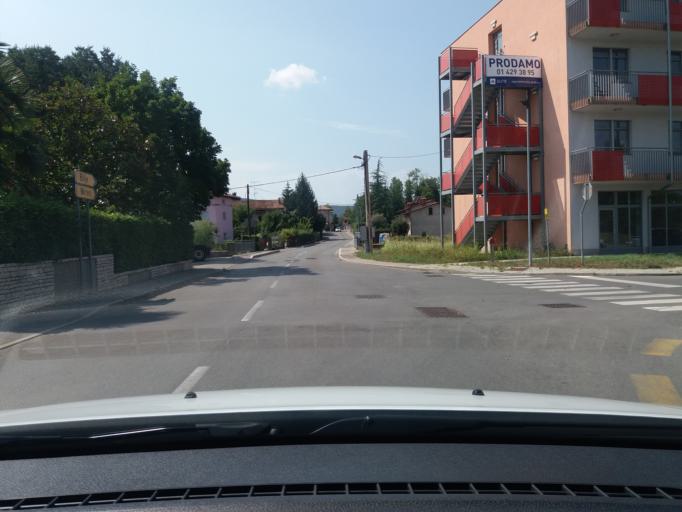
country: SI
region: Sempeter-Vrtojba
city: Vrtojba
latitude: 45.9067
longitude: 13.6294
